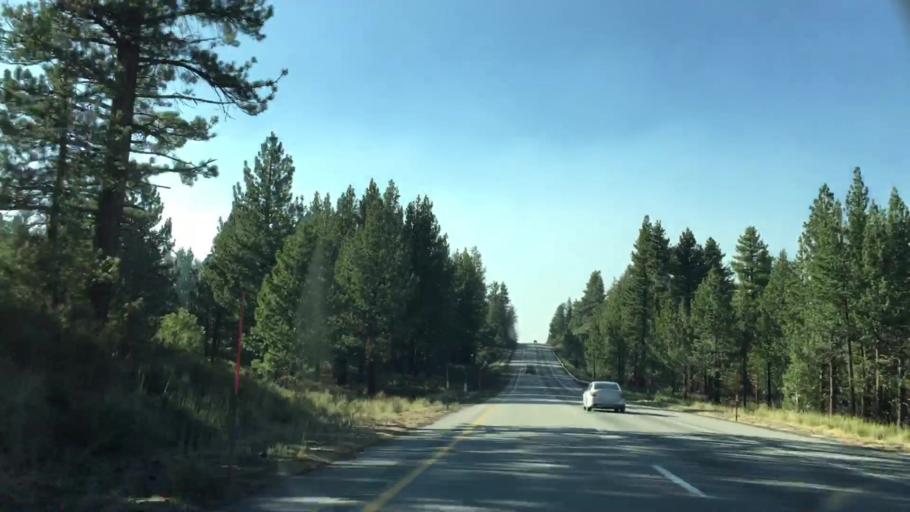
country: US
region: California
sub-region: Mono County
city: Mammoth Lakes
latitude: 37.7192
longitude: -118.9583
